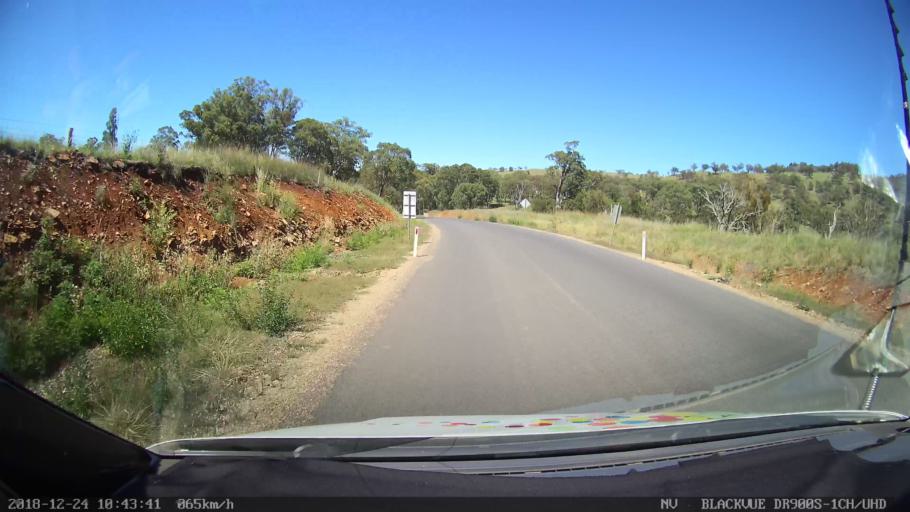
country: AU
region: New South Wales
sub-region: Upper Hunter Shire
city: Merriwa
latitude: -31.8845
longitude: 150.4447
